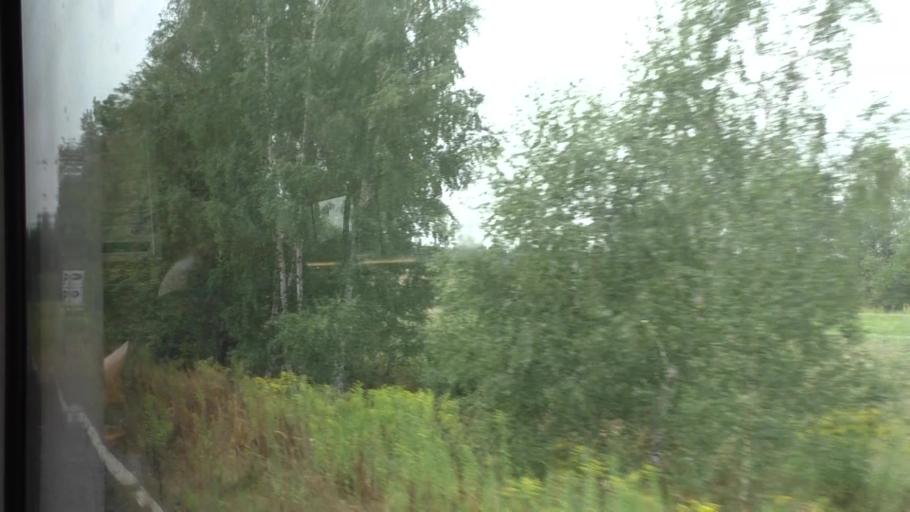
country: DE
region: Saxony
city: Hirschfelde
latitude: 50.9360
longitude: 14.8770
